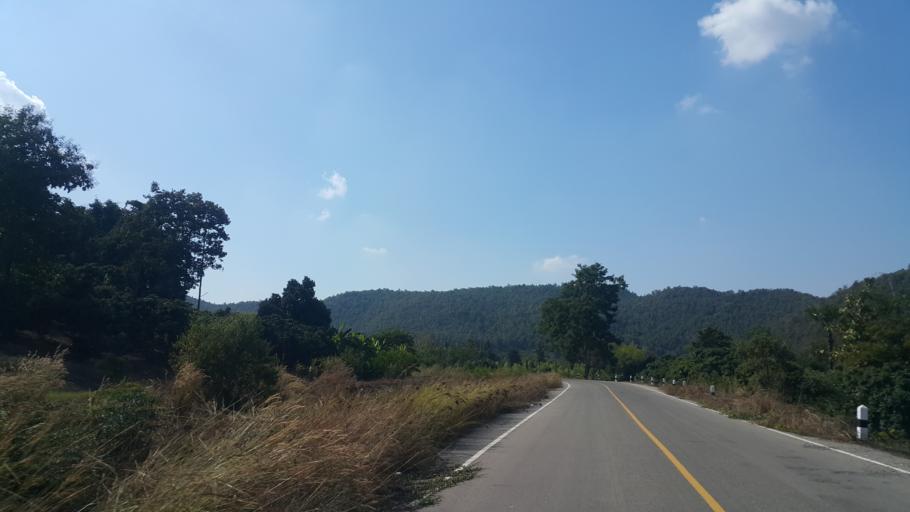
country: TH
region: Lamphun
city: Ban Thi
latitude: 18.6235
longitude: 99.1540
